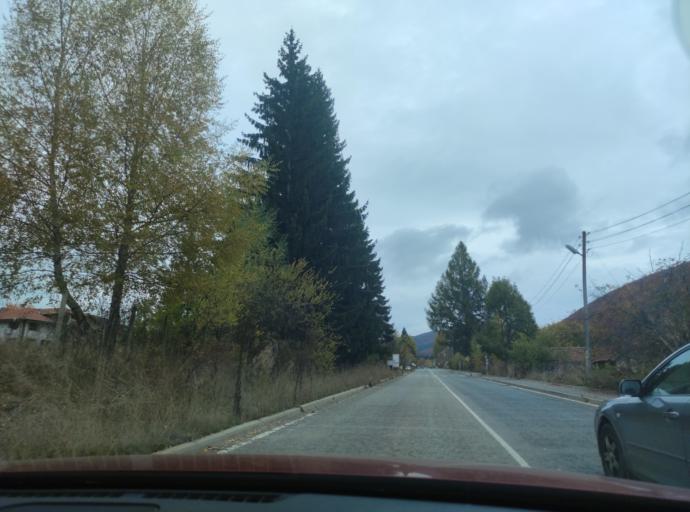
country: BG
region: Sofiya
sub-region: Obshtina Godech
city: Godech
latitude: 43.0931
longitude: 23.0986
